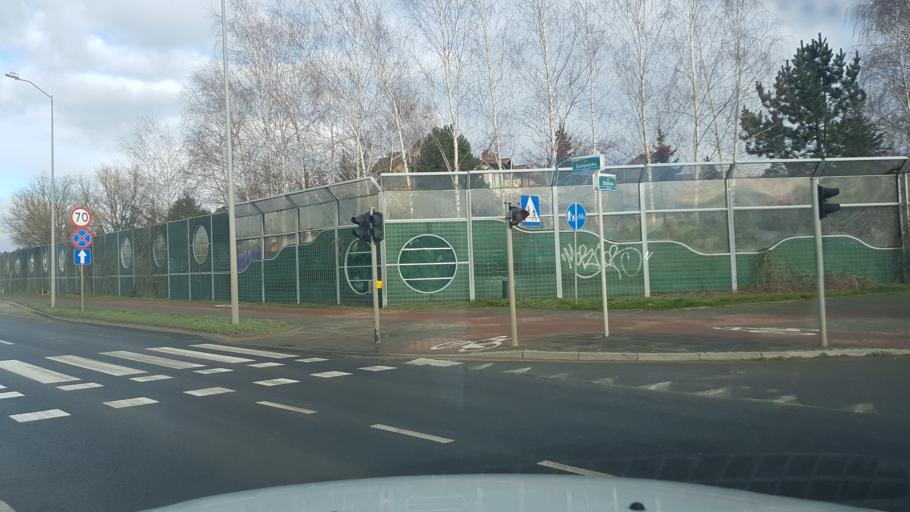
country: PL
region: West Pomeranian Voivodeship
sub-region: Powiat policki
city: Przeclaw
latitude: 53.4095
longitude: 14.4909
